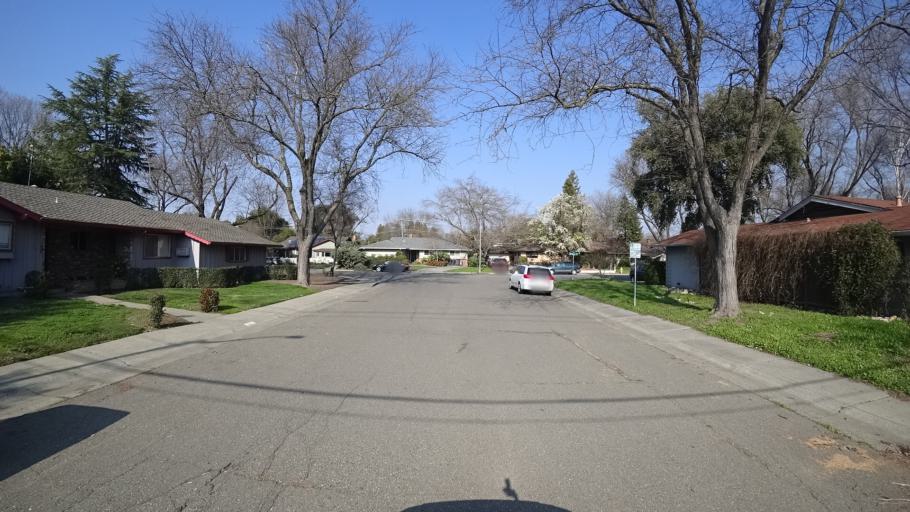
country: US
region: California
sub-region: Yolo County
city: Davis
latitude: 38.5526
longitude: -121.7514
